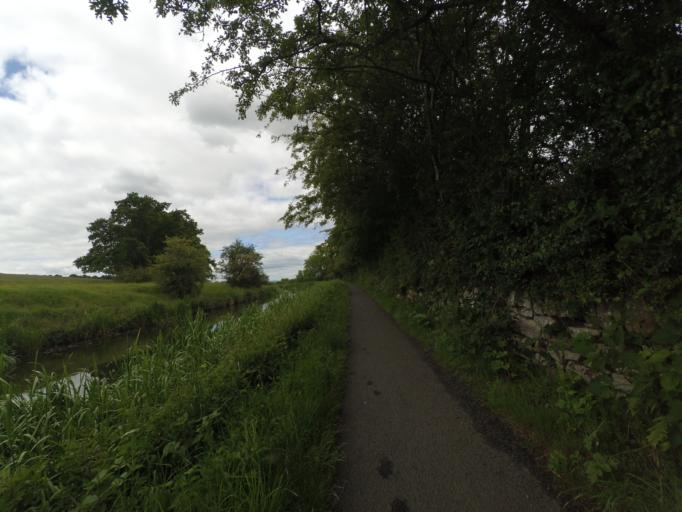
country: GB
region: Scotland
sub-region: Falkirk
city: Polmont
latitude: 55.9829
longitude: -3.6991
